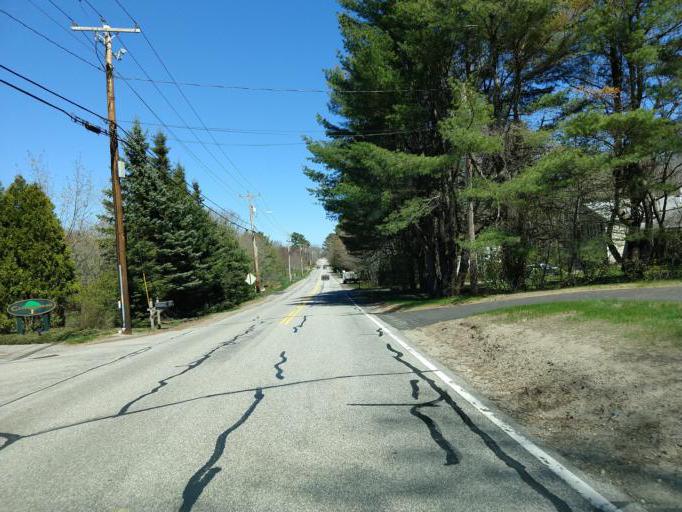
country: US
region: Maine
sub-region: York County
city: Kennebunkport
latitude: 43.3551
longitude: -70.5030
